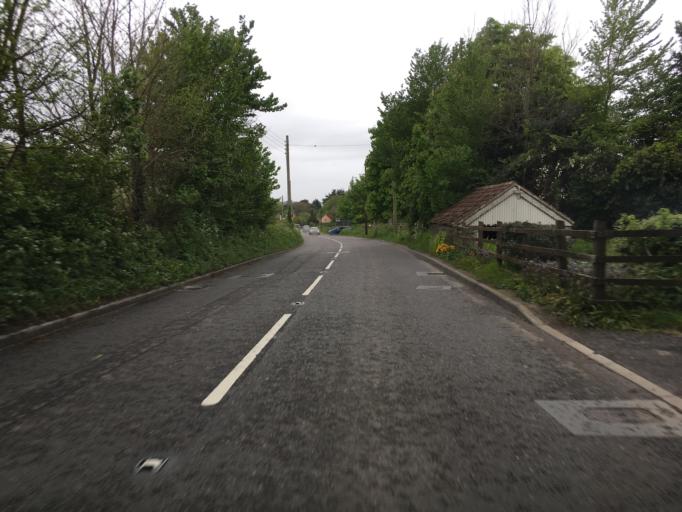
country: GB
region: England
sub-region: North Somerset
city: Churchill
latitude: 51.3332
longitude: -2.8068
